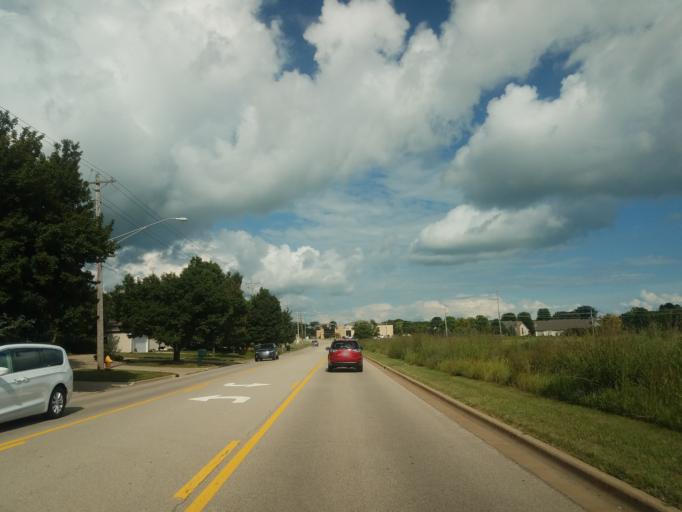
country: US
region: Illinois
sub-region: McLean County
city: Normal
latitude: 40.5103
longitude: -88.9270
